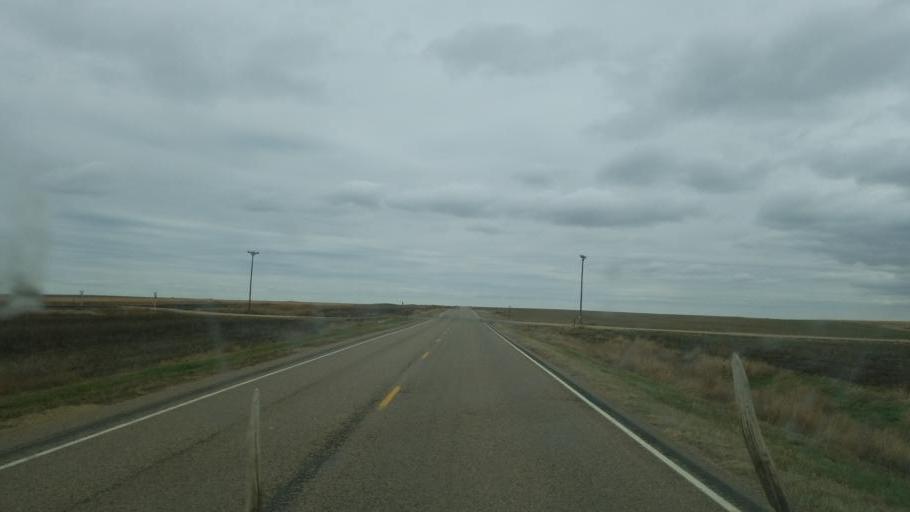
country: US
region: Colorado
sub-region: Cheyenne County
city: Cheyenne Wells
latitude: 38.8429
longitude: -102.2602
